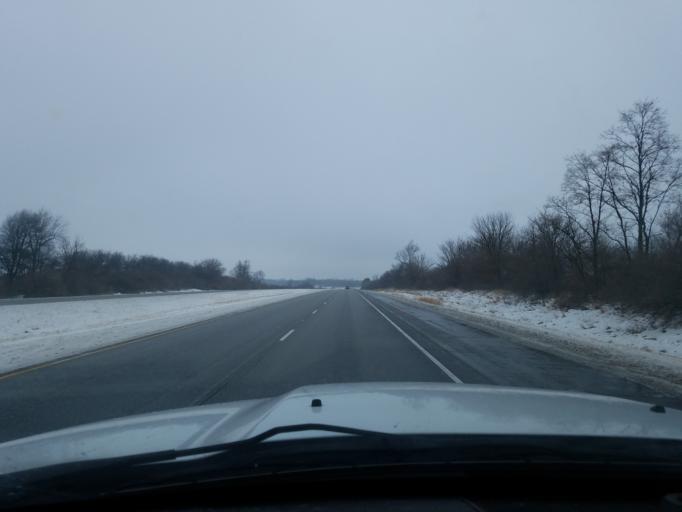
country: US
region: Indiana
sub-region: Fulton County
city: Rochester
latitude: 40.9222
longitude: -86.1619
